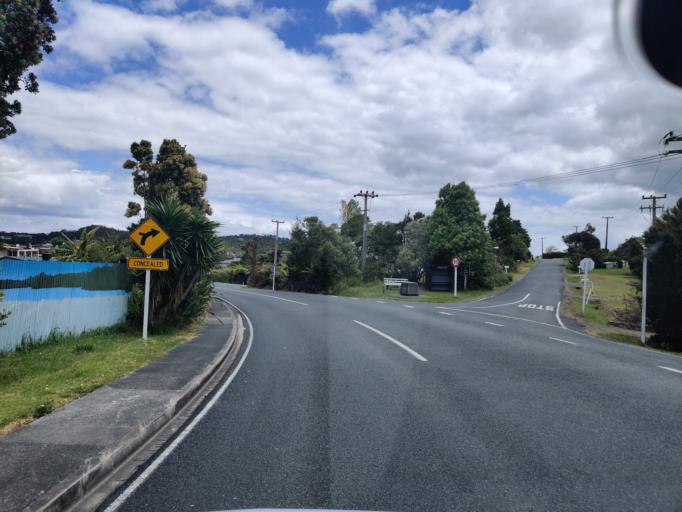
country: NZ
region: Northland
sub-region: Far North District
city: Paihia
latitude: -35.3039
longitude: 174.1223
